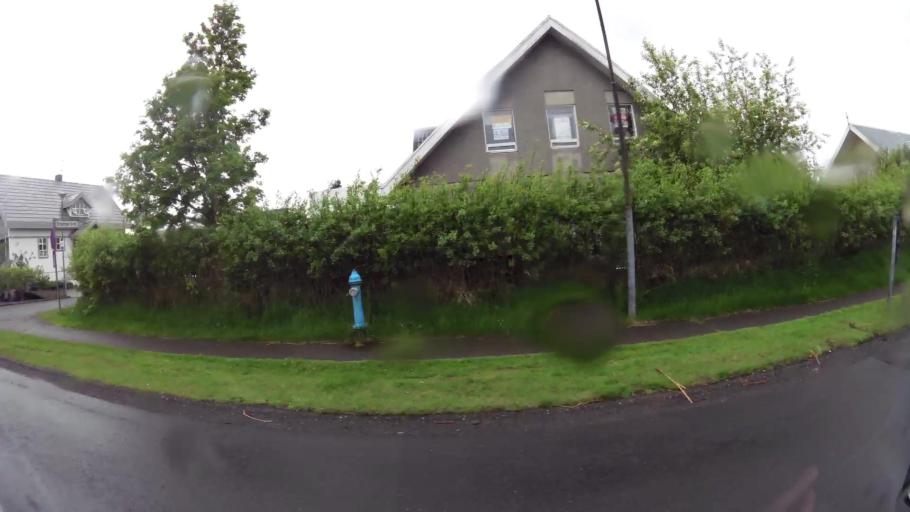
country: IS
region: Capital Region
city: Gardabaer
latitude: 64.0930
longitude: -21.9164
